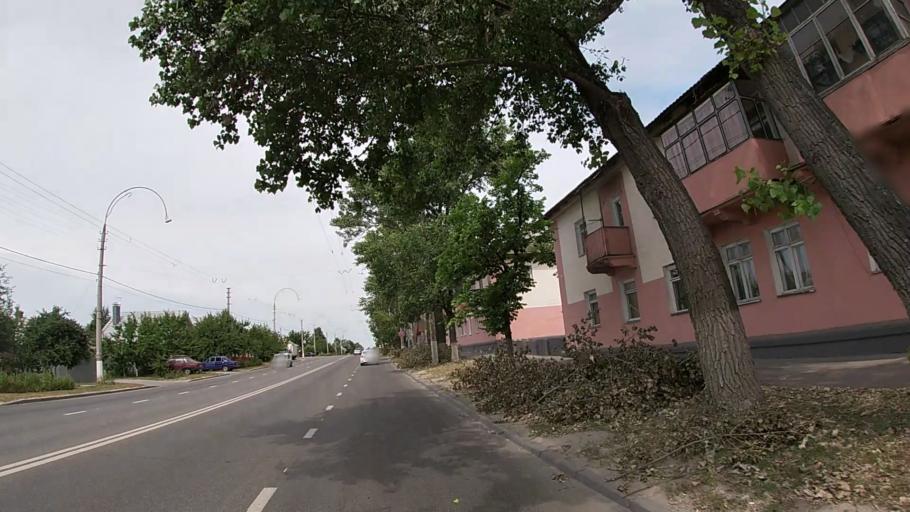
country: RU
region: Belgorod
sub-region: Belgorodskiy Rayon
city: Belgorod
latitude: 50.6063
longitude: 36.5527
